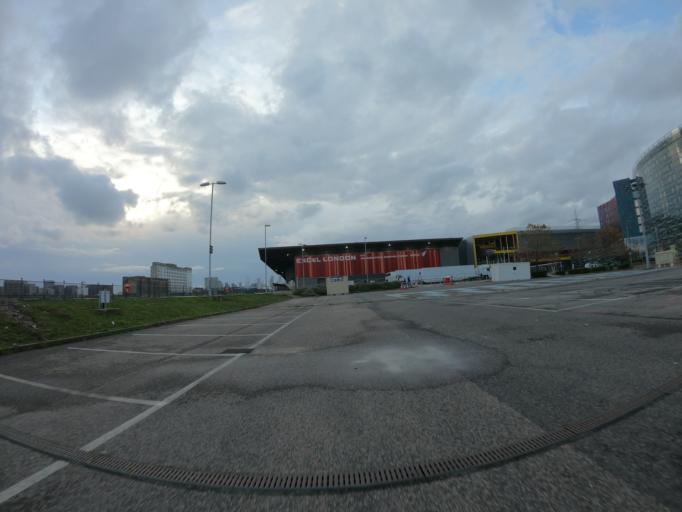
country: GB
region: England
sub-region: Greater London
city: East Ham
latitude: 51.5075
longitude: 0.0364
